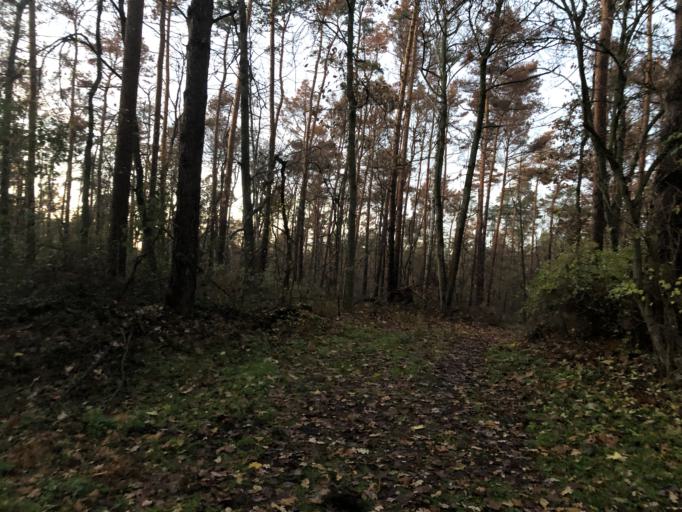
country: DE
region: Saxony-Anhalt
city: Halle Neustadt
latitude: 51.4920
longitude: 11.8909
